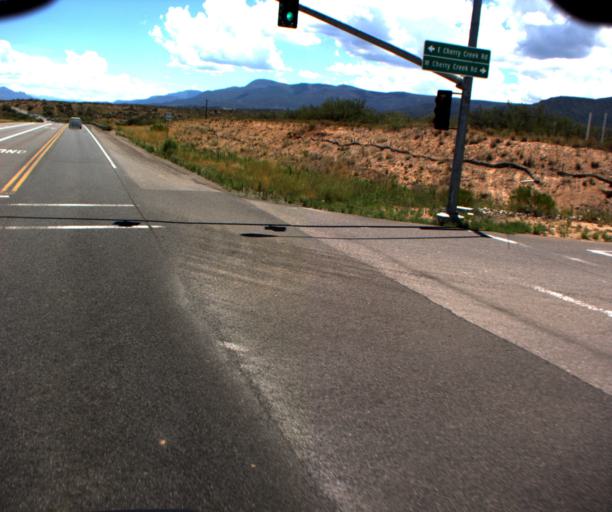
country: US
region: Arizona
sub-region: Yavapai County
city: Camp Verde
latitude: 34.6094
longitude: -111.9120
